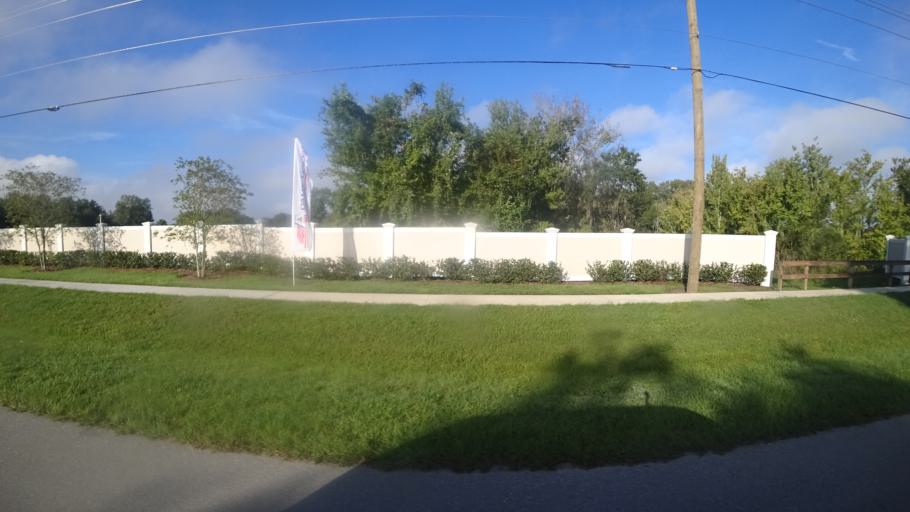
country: US
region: Florida
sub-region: Manatee County
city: Ellenton
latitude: 27.5531
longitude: -82.4664
